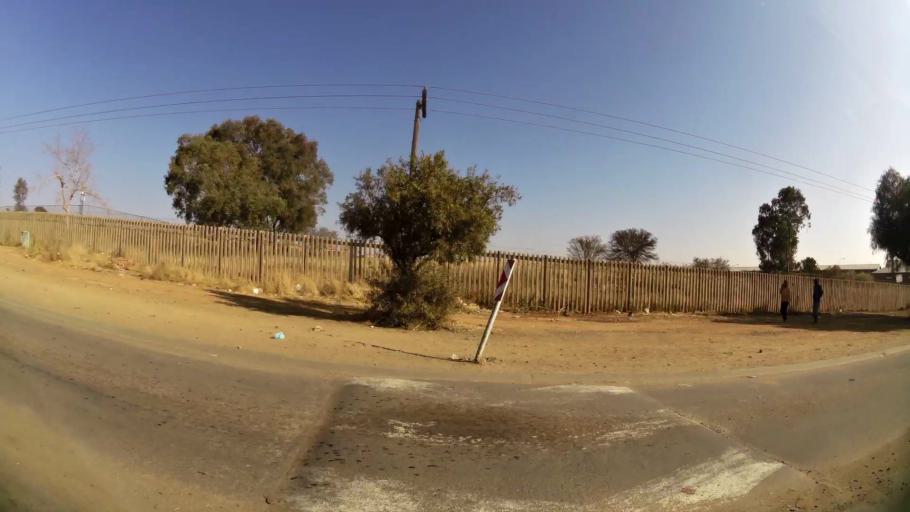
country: ZA
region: Orange Free State
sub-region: Mangaung Metropolitan Municipality
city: Bloemfontein
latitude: -29.1861
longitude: 26.2225
